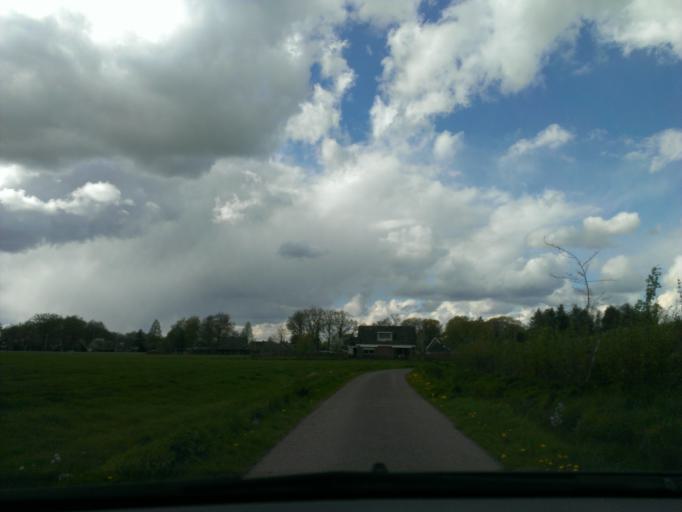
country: NL
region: Gelderland
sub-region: Gemeente Voorst
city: Twello
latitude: 52.2343
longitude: 6.0527
